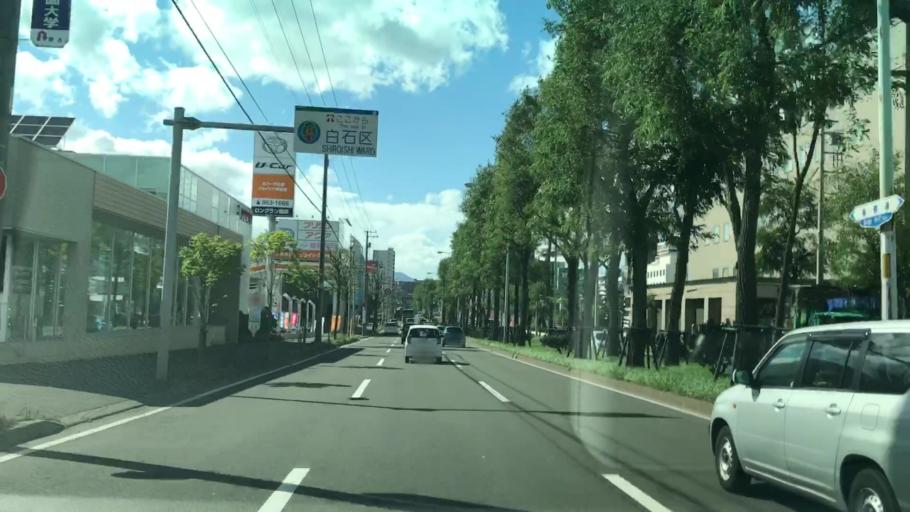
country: JP
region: Hokkaido
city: Sapporo
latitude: 43.0281
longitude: 141.4440
